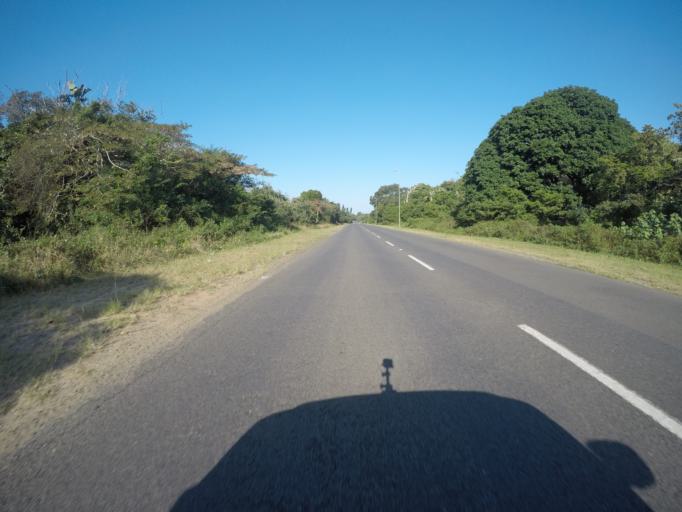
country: ZA
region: KwaZulu-Natal
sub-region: uThungulu District Municipality
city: Richards Bay
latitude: -28.7884
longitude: 32.0874
